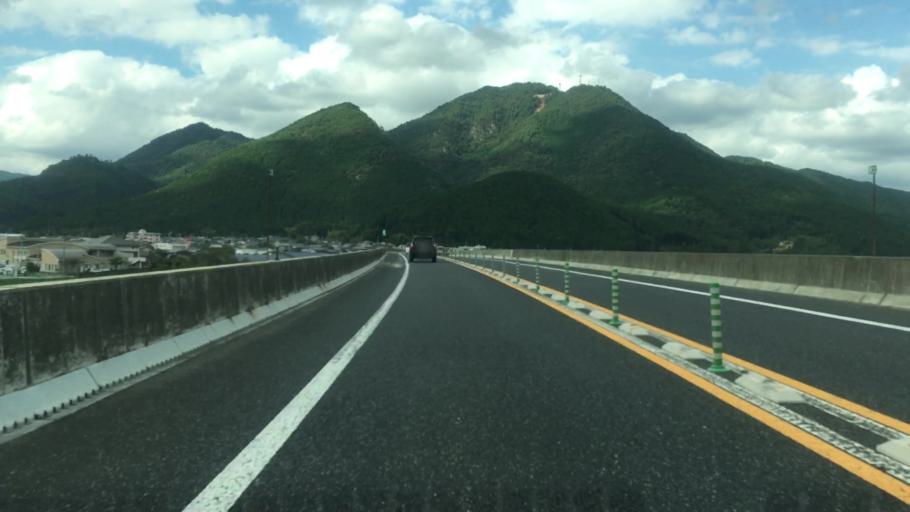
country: JP
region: Kyoto
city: Fukuchiyama
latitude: 35.1771
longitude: 135.0391
